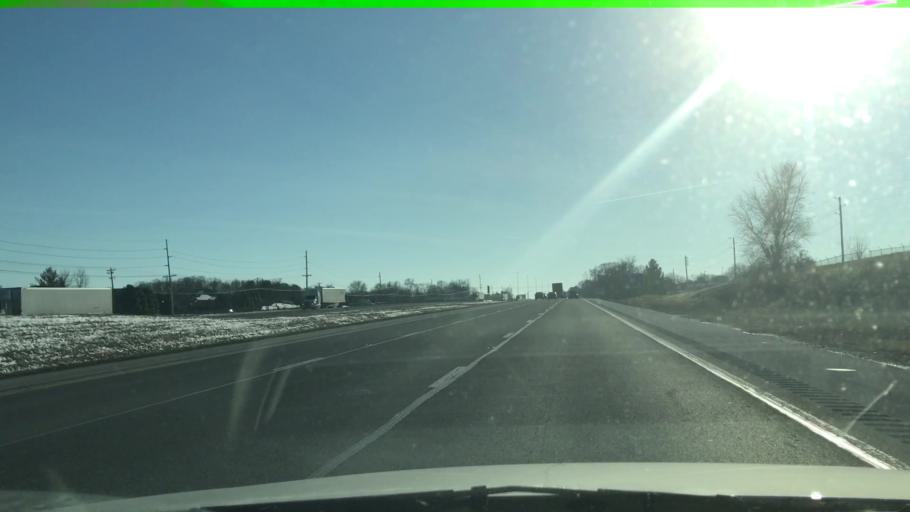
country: US
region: Kentucky
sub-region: Warren County
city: Bowling Green
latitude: 36.9565
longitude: -86.4042
